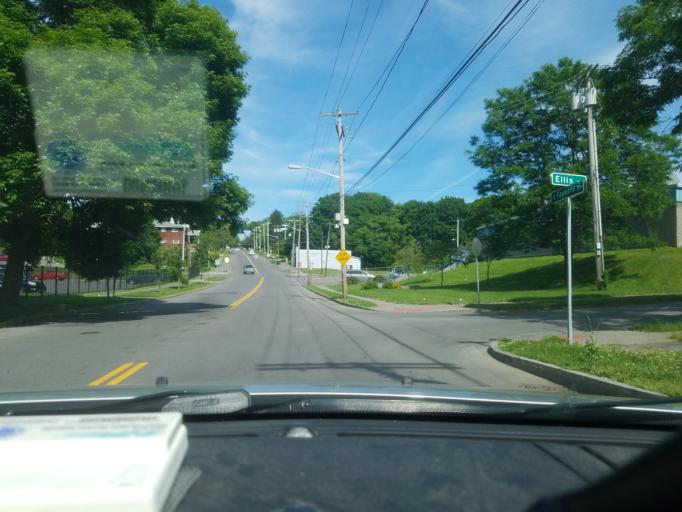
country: US
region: New York
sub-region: Onondaga County
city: Syracuse
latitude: 43.0481
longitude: -76.1139
